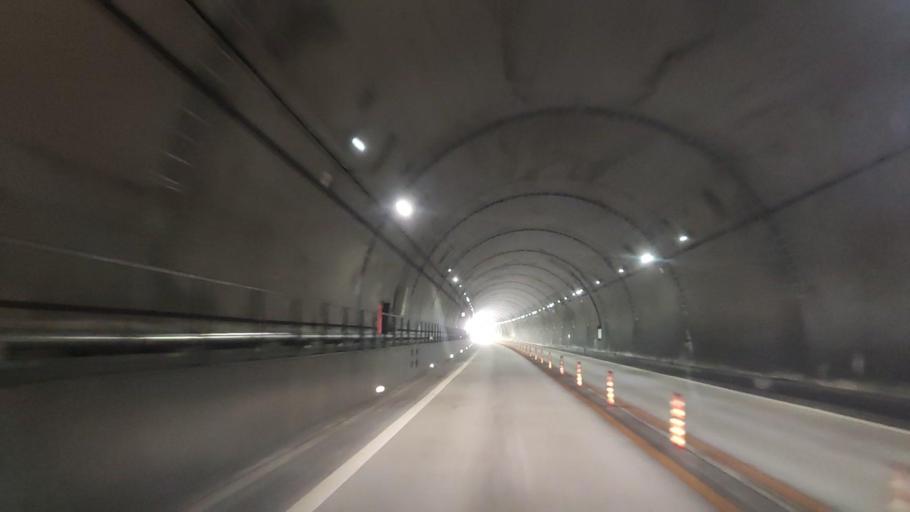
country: JP
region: Ehime
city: Hojo
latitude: 34.0855
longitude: 132.9779
